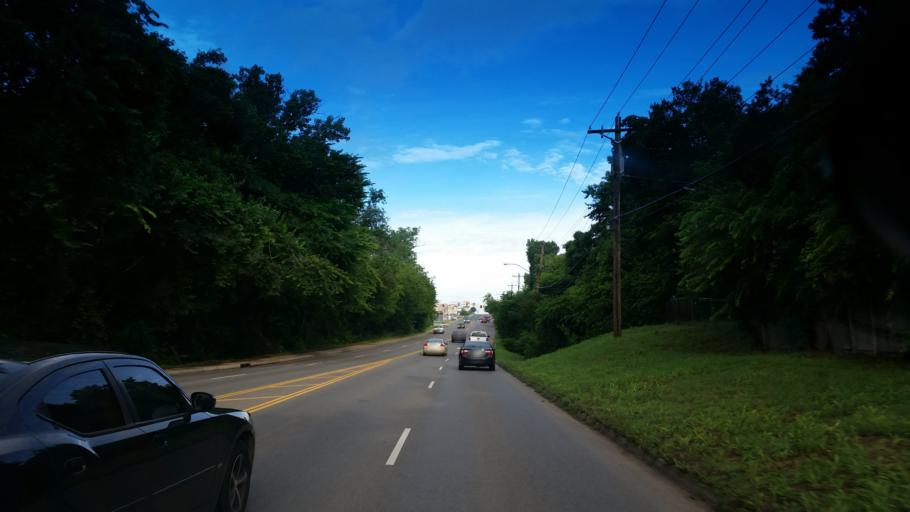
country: US
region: Oklahoma
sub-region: Oklahoma County
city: Edmond
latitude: 35.6384
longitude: -97.4748
